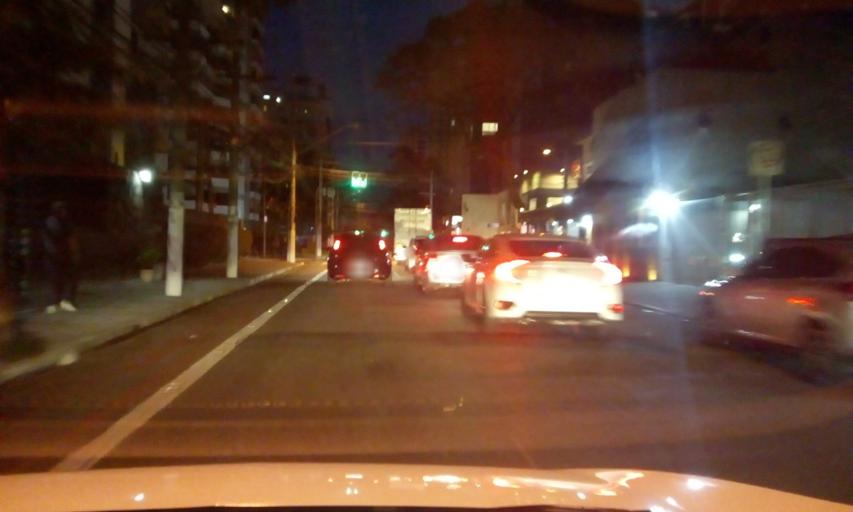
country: BR
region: Sao Paulo
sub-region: Sao Paulo
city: Sao Paulo
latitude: -23.6017
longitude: -46.6725
